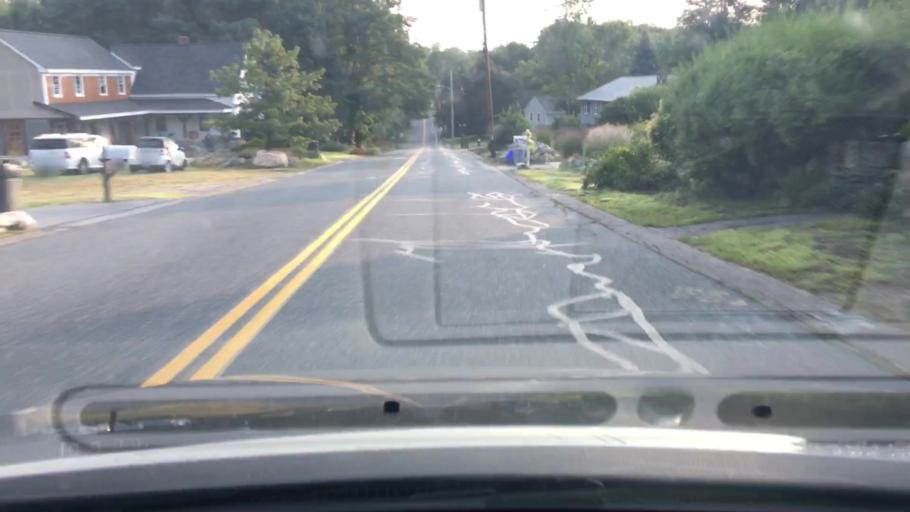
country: US
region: Massachusetts
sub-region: Worcester County
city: Milford
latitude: 42.1675
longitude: -71.5353
